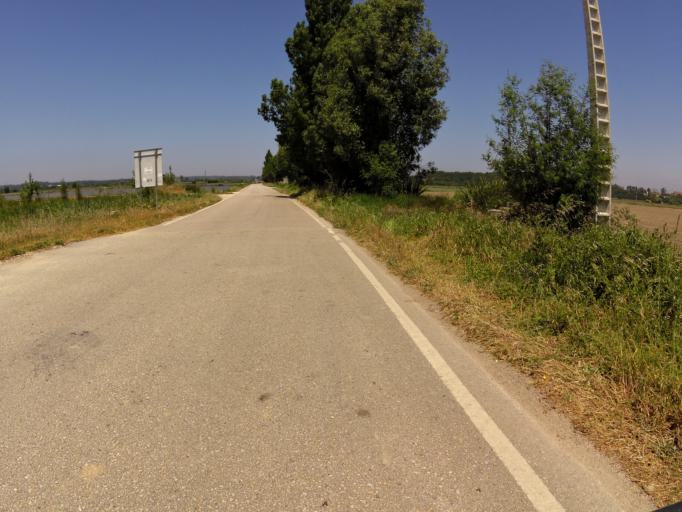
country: PT
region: Coimbra
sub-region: Montemor-O-Velho
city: Montemor-o-Velho
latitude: 40.1610
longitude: -8.7151
